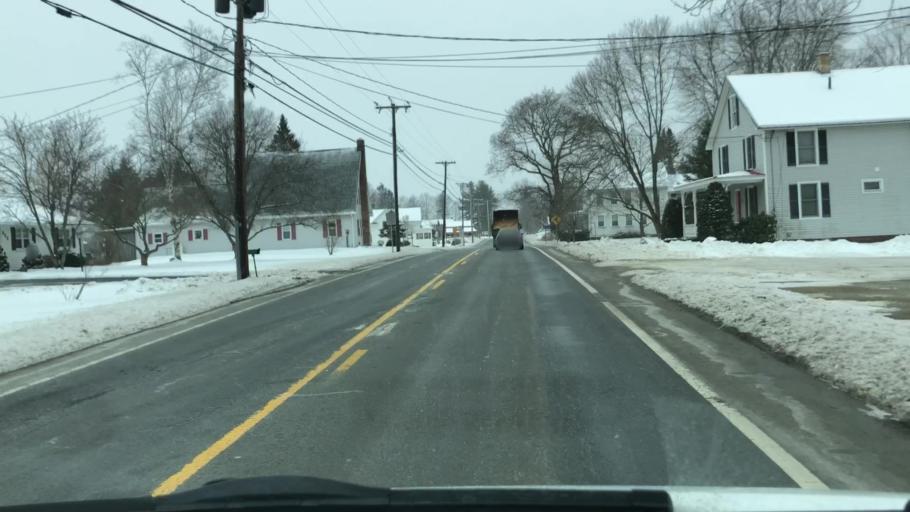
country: US
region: Massachusetts
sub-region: Franklin County
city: Whately
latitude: 42.4109
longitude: -72.6230
